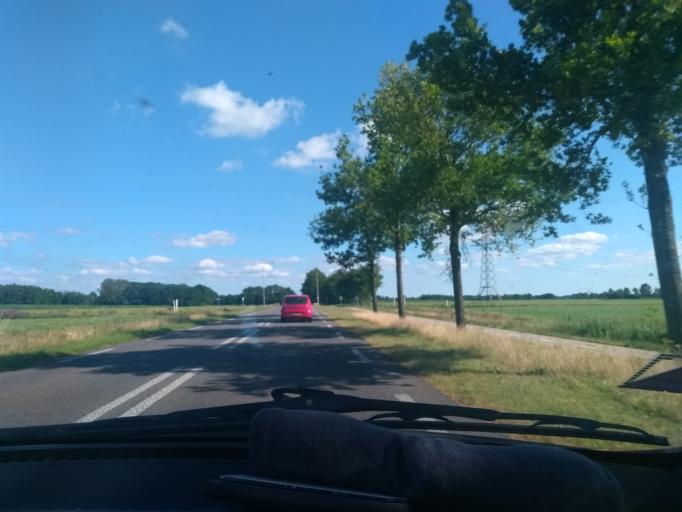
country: NL
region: Drenthe
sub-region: Gemeente Tynaarlo
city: Vries
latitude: 53.1191
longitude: 6.5089
